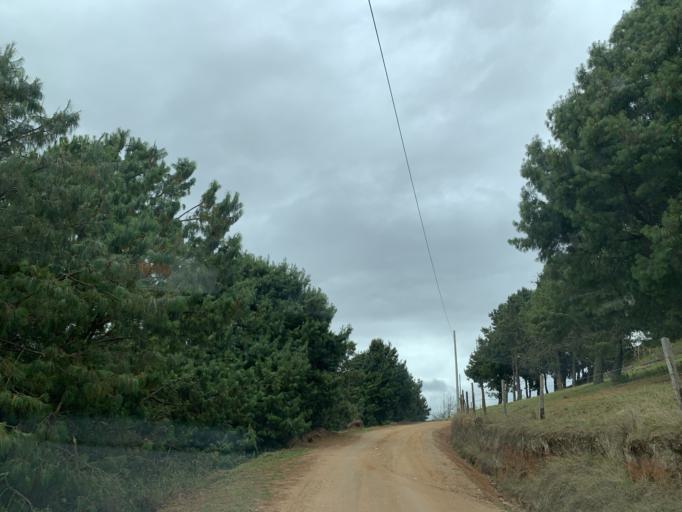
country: CO
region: Boyaca
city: Tunja
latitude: 5.5294
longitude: -73.3196
